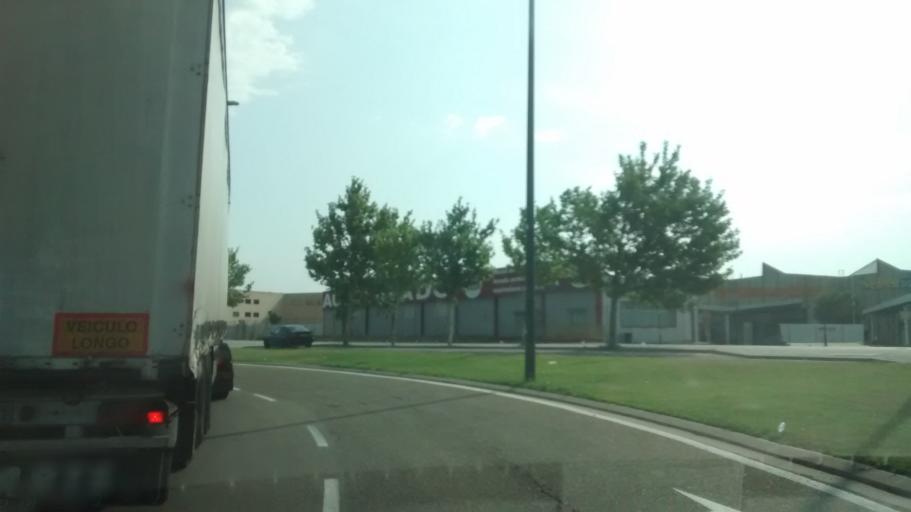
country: ES
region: Aragon
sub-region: Provincia de Zaragoza
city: Zaragoza
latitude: 41.6673
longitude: -0.8589
